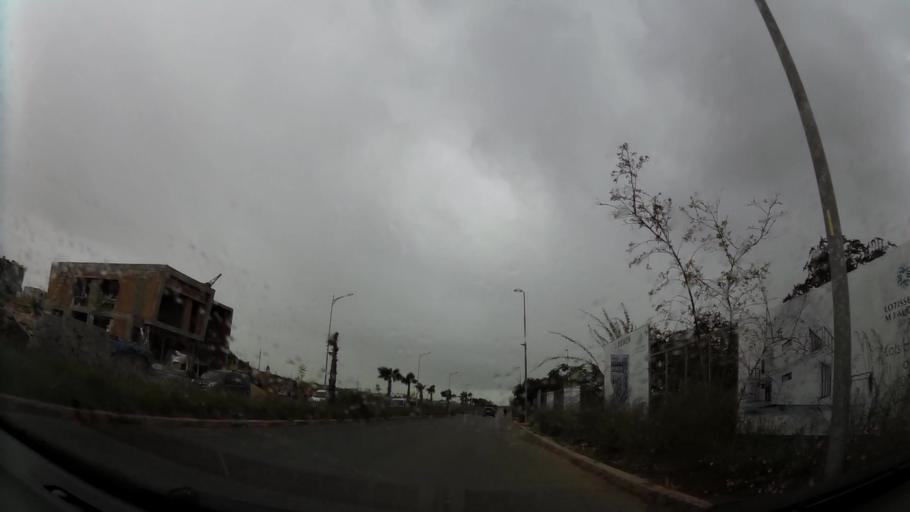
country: MA
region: Grand Casablanca
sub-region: Casablanca
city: Casablanca
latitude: 33.5241
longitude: -7.6226
